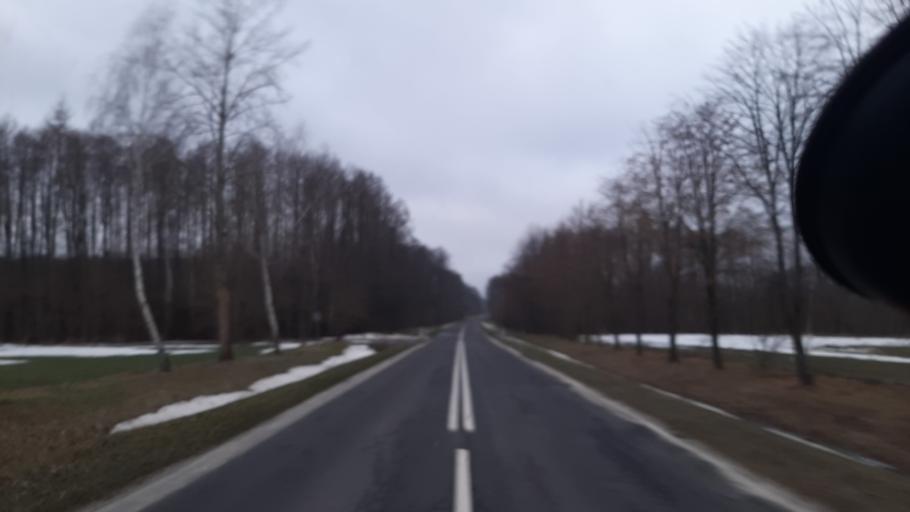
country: PL
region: Lublin Voivodeship
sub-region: Powiat wlodawski
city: Hansk
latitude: 51.5611
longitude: 23.3420
